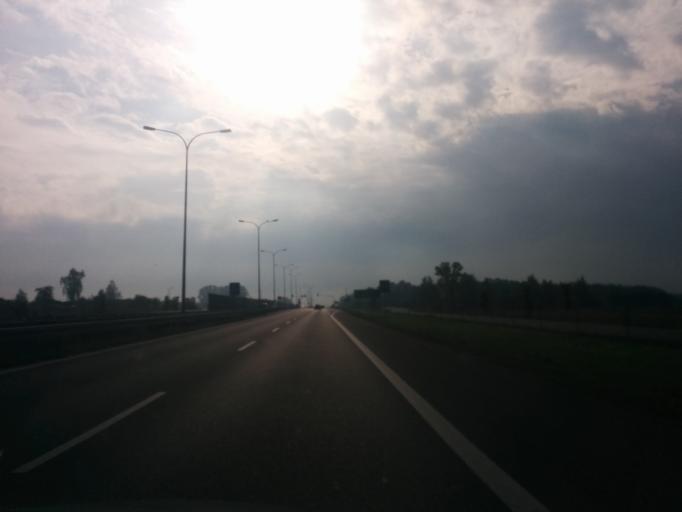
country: PL
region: Masovian Voivodeship
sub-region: Powiat radomski
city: Jedlinsk
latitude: 51.5327
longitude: 21.0795
